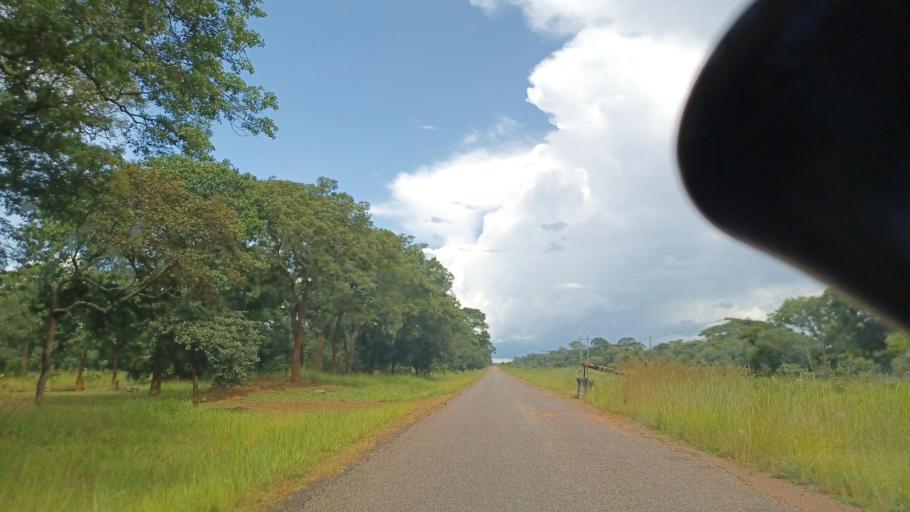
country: ZM
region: North-Western
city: Kasempa
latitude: -12.8913
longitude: 26.0508
